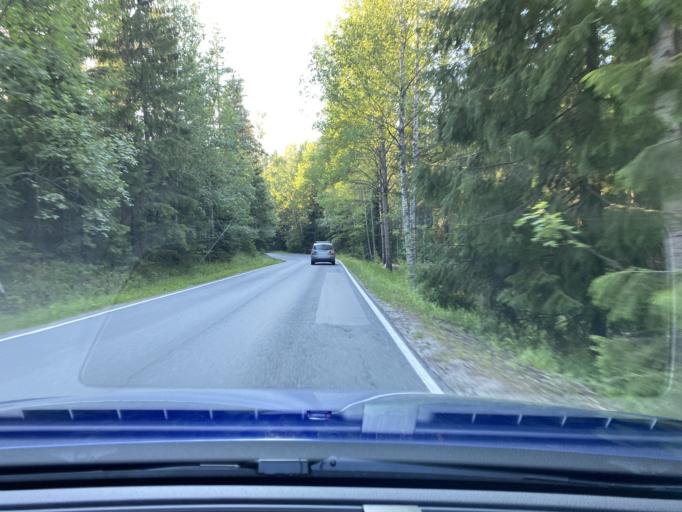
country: FI
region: Haeme
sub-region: Riihimaeki
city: Riihimaeki
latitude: 60.7279
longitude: 24.6947
